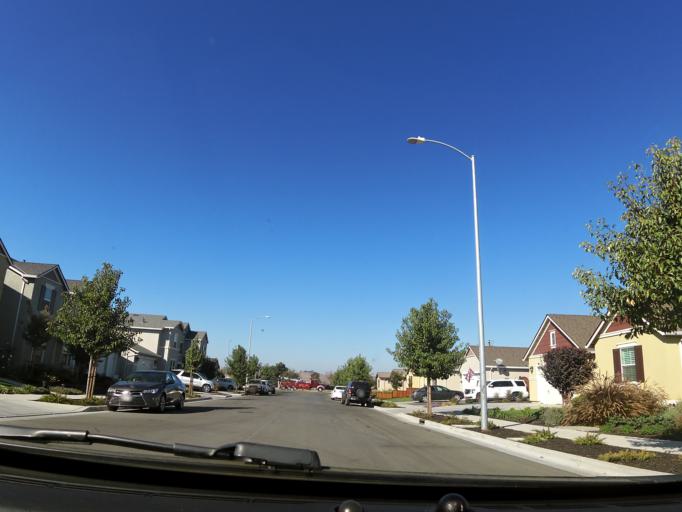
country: US
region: California
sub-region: San Benito County
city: Hollister
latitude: 36.8325
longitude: -121.3997
